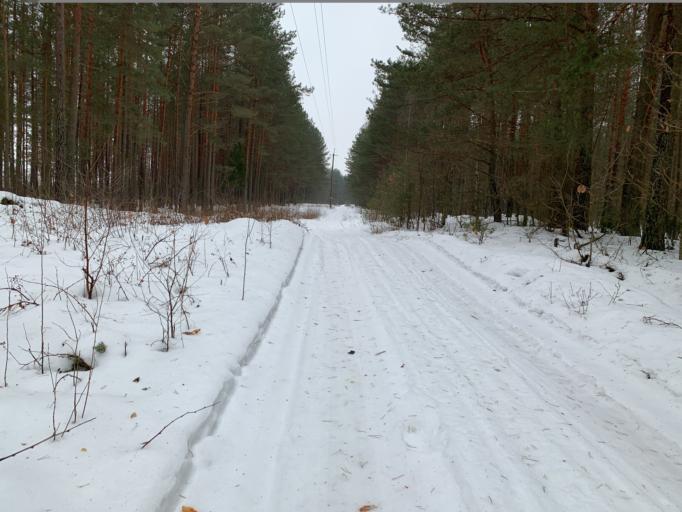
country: BY
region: Minsk
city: Il'ya
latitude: 54.5433
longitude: 27.2767
